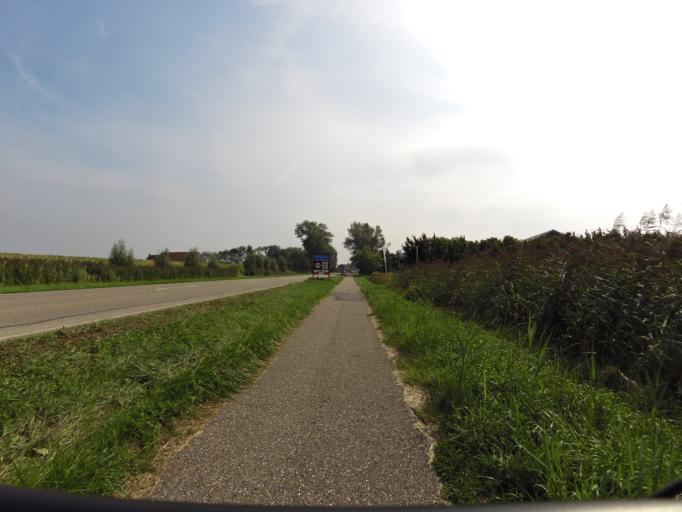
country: NL
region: Zeeland
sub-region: Gemeente Middelburg
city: Middelburg
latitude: 51.5334
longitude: 3.6041
